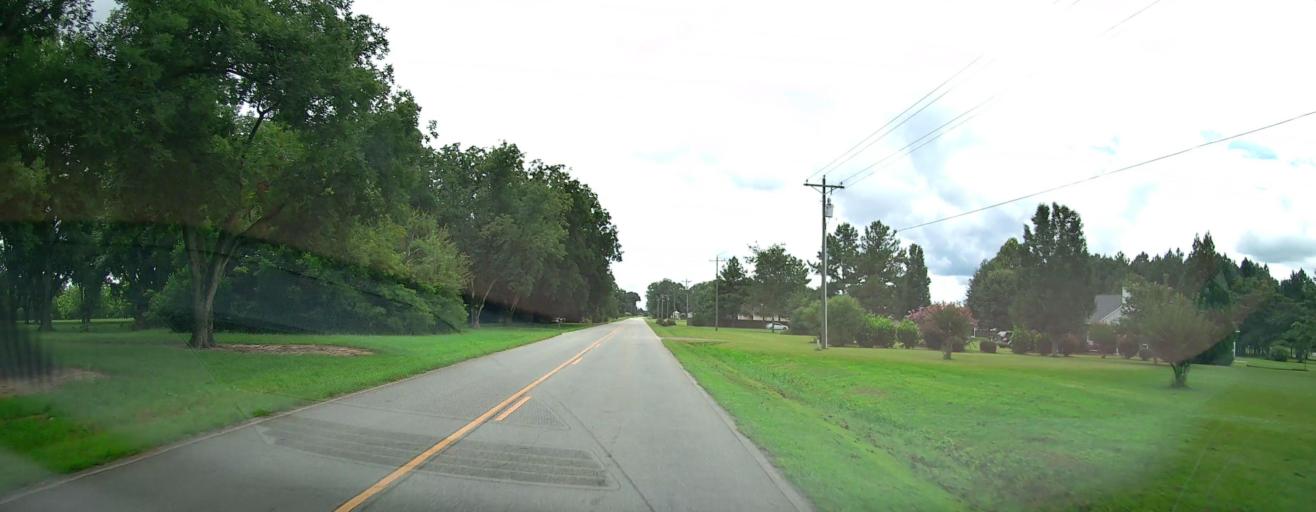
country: US
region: Georgia
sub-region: Peach County
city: Byron
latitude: 32.5616
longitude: -83.7534
